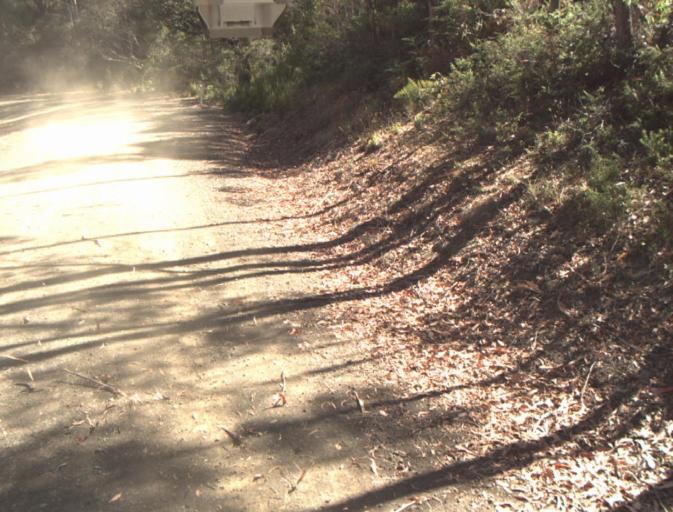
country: AU
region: Tasmania
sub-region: Launceston
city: Newstead
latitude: -41.3083
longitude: 147.3354
